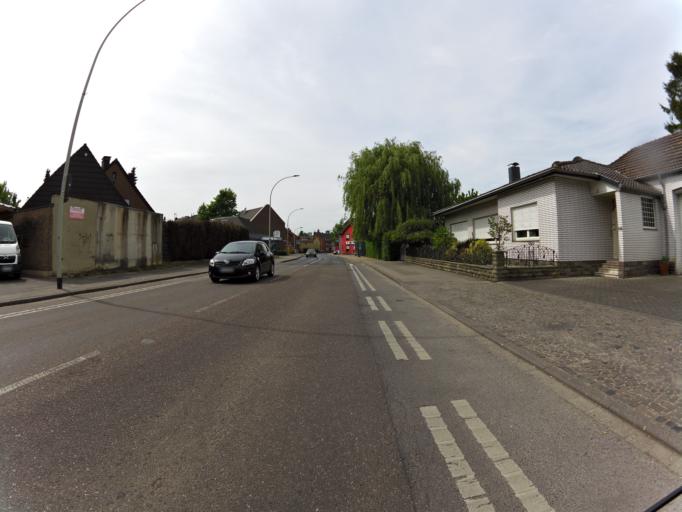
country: DE
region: North Rhine-Westphalia
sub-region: Regierungsbezirk Koln
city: Wurselen
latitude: 50.8375
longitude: 6.1174
